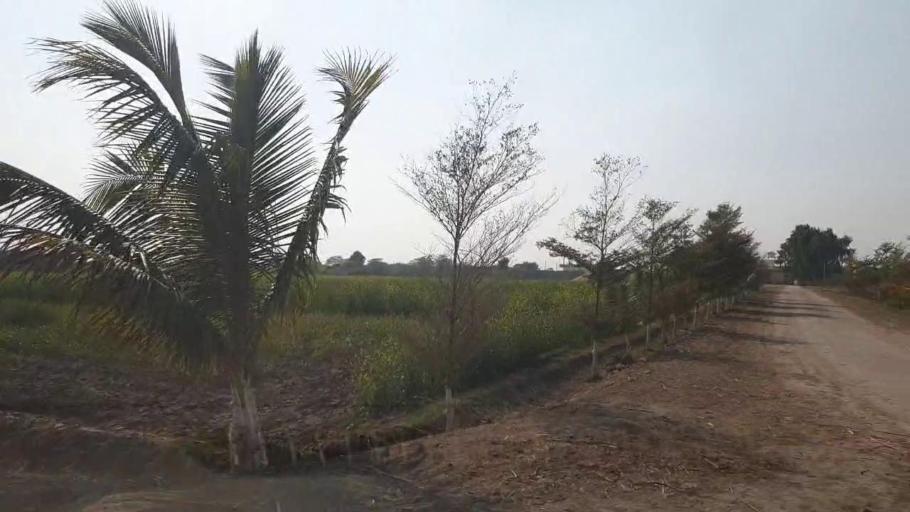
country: PK
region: Sindh
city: Mirwah Gorchani
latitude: 25.2837
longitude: 68.9474
